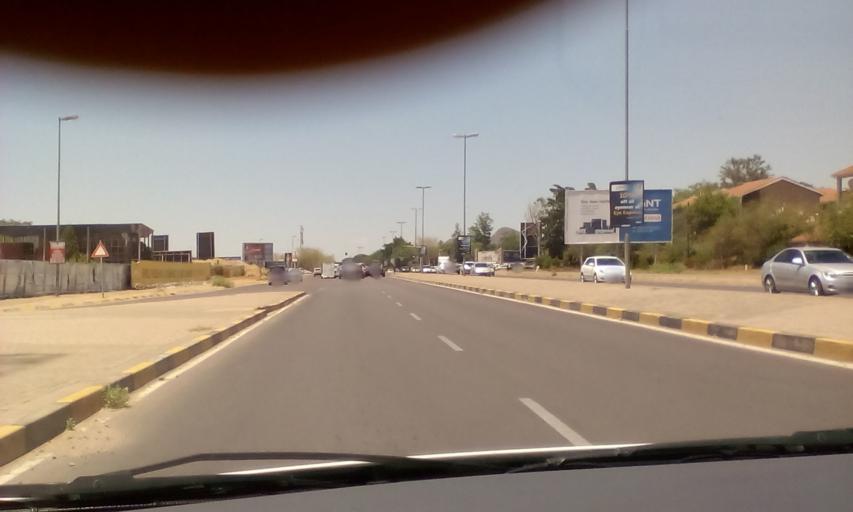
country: BW
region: South East
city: Gaborone
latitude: -24.6532
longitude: 25.9016
